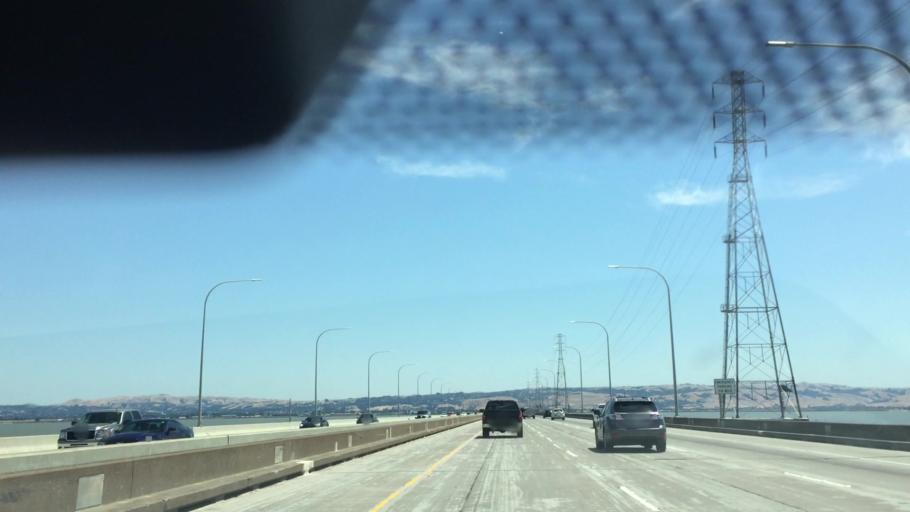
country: US
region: California
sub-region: San Mateo County
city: Foster City
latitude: 37.6064
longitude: -122.1892
